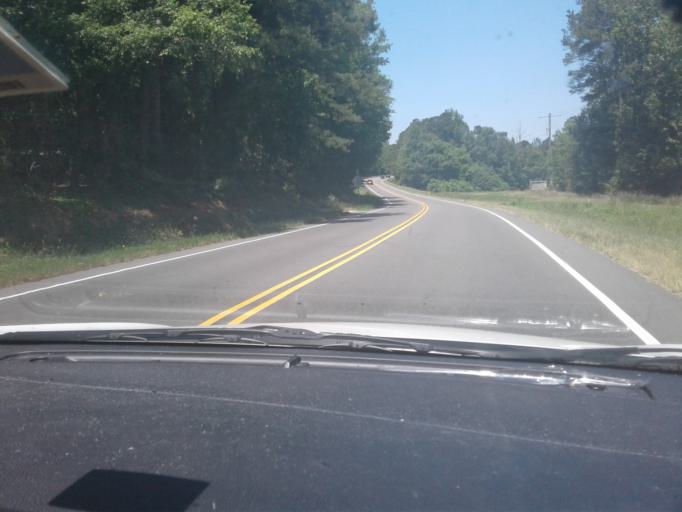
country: US
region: North Carolina
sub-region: Harnett County
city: Lillington
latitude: 35.4268
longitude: -78.8180
